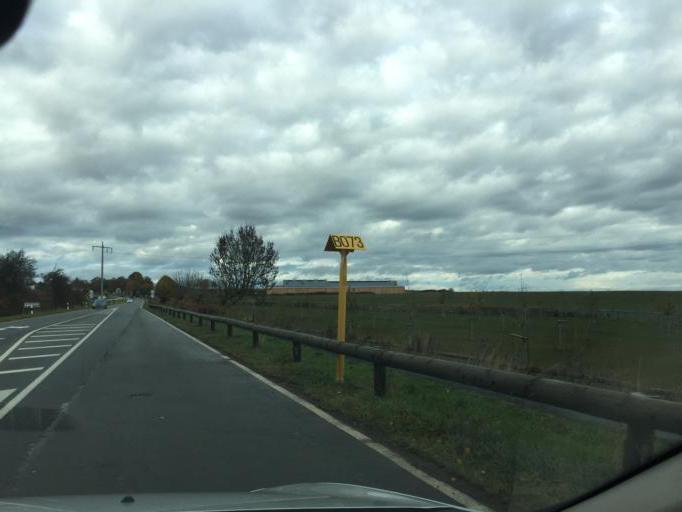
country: LU
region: Diekirch
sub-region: Canton de Wiltz
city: Goesdorf
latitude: 49.8805
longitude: 5.9904
